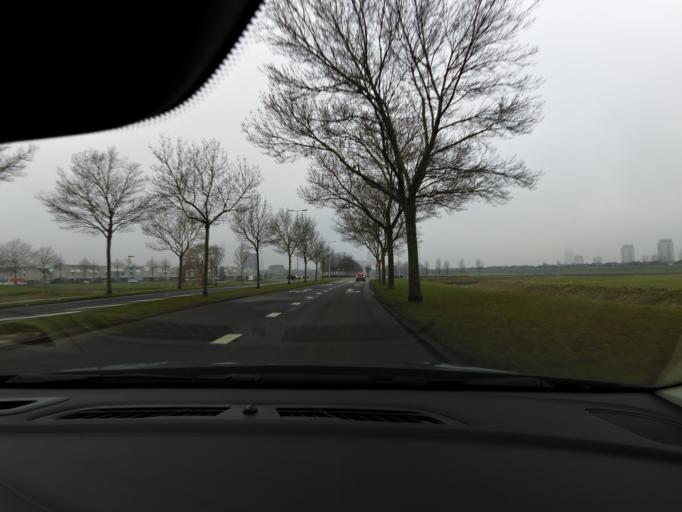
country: NL
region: South Holland
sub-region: Gemeente Spijkenisse
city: Spijkenisse
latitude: 51.8393
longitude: 4.3583
